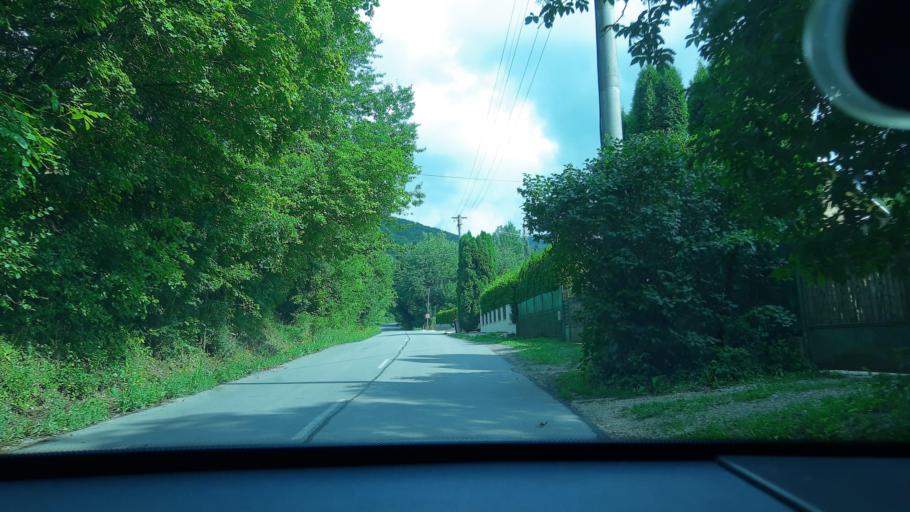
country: SK
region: Trnavsky
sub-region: Okres Trnava
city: Piestany
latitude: 48.6505
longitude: 17.9411
